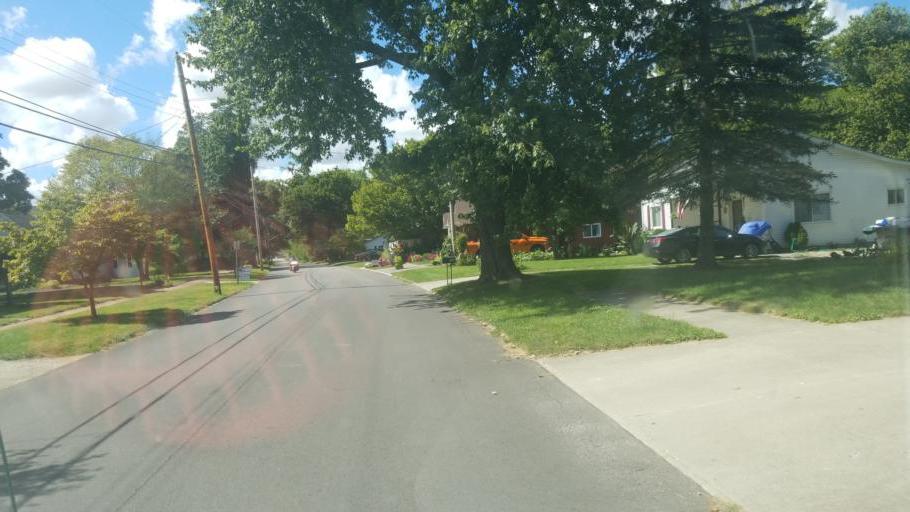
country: US
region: Ohio
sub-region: Union County
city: Marysville
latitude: 40.1805
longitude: -83.4402
